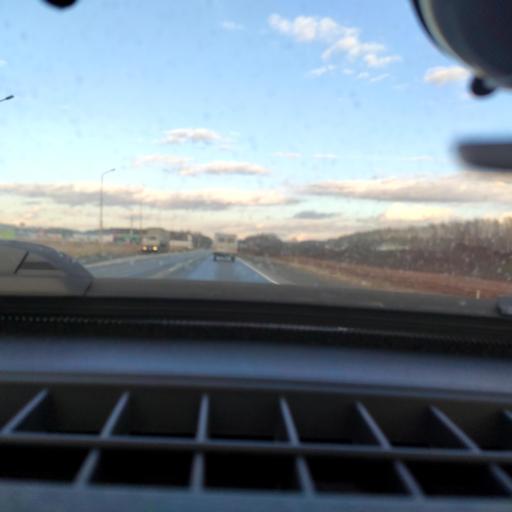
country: RU
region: Bashkortostan
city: Iglino
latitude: 54.7373
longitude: 56.2846
